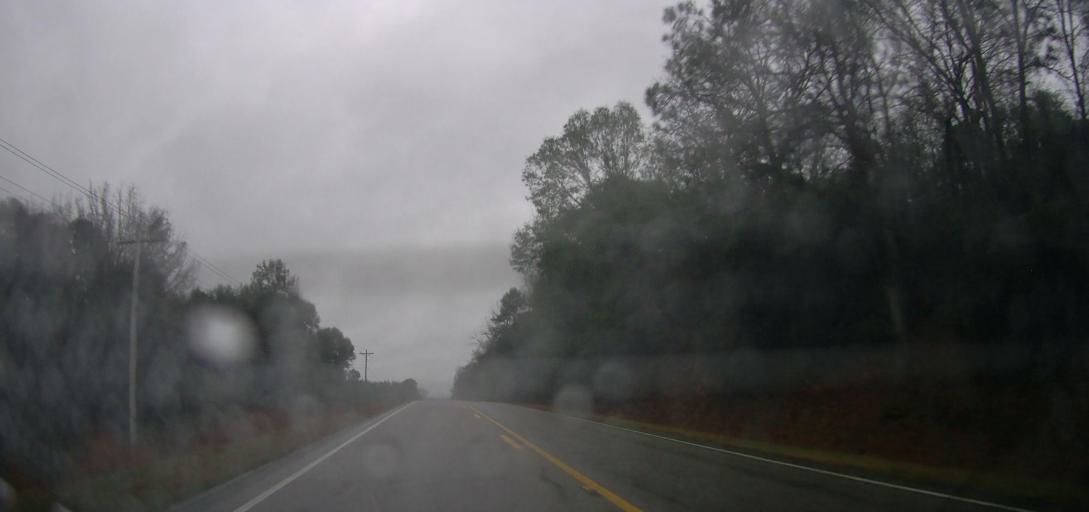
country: US
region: Alabama
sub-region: Autauga County
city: Pine Level
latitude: 32.5308
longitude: -86.6351
